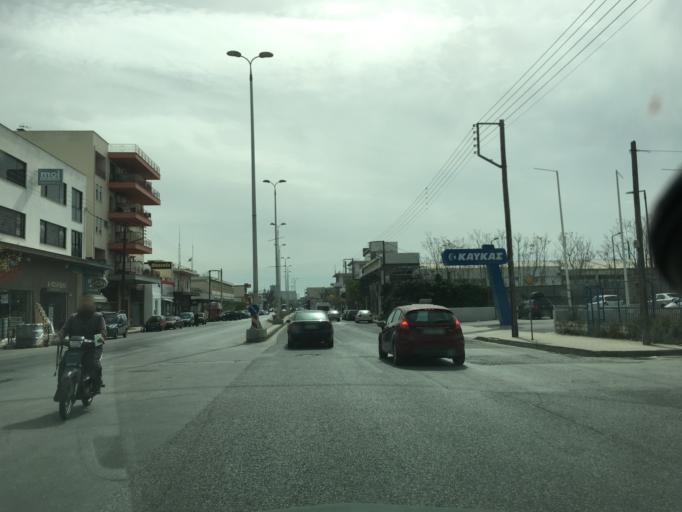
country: GR
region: Thessaly
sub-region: Nomos Magnisias
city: Nea Ionia
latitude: 39.3646
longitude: 22.9274
